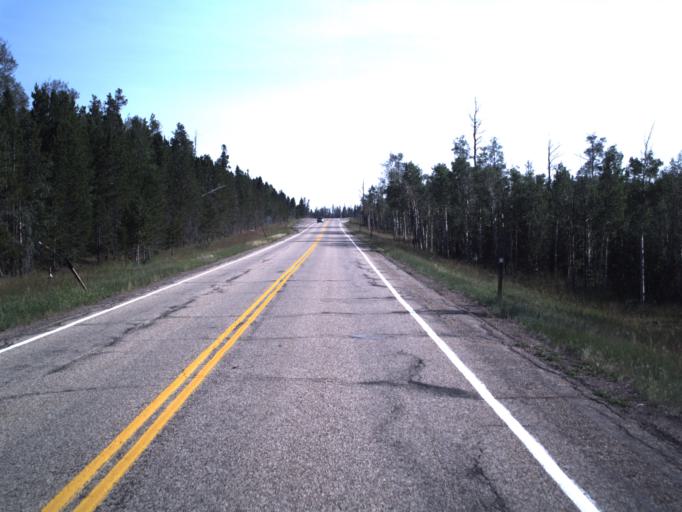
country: US
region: Utah
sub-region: Daggett County
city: Manila
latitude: 40.8103
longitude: -109.4673
